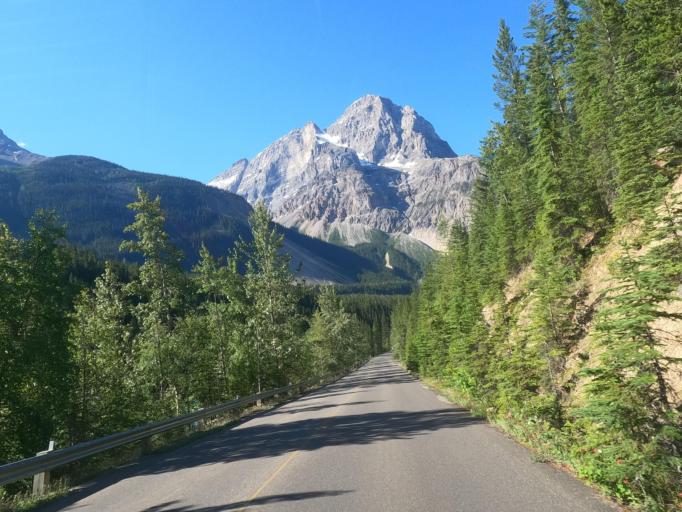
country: CA
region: Alberta
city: Lake Louise
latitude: 51.4317
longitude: -116.4227
